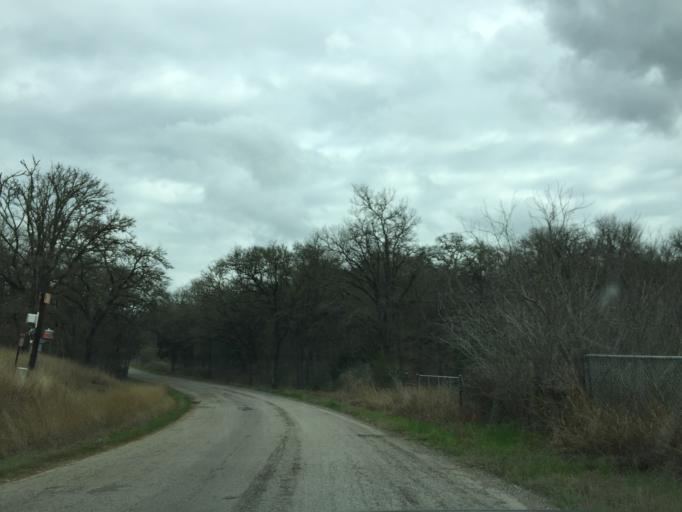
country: US
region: Texas
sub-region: Bastrop County
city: Bastrop
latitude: 30.1229
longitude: -97.3047
